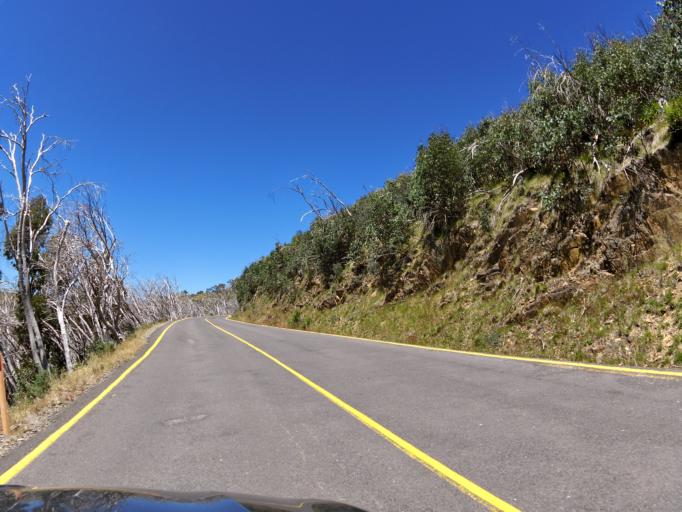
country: AU
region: Victoria
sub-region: Alpine
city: Mount Beauty
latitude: -37.0053
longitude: 147.0759
